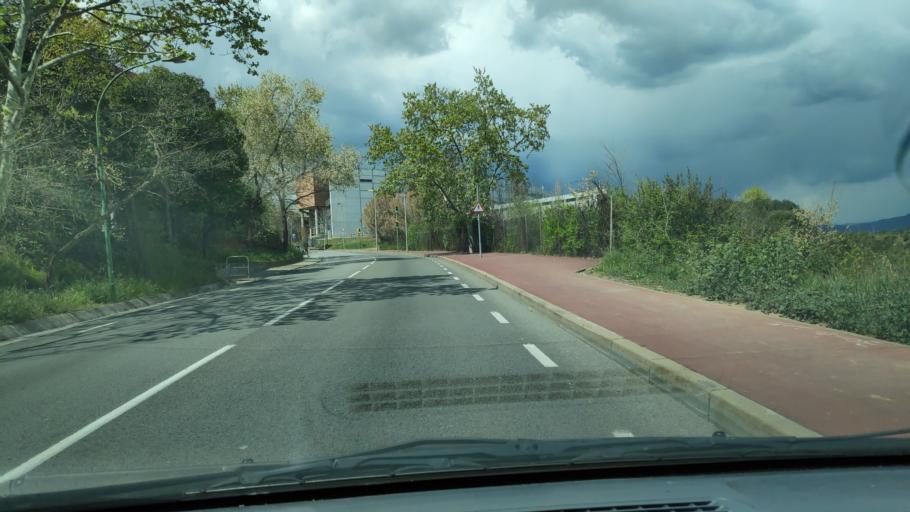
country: ES
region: Catalonia
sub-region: Provincia de Barcelona
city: Sabadell
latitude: 41.5454
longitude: 2.1206
